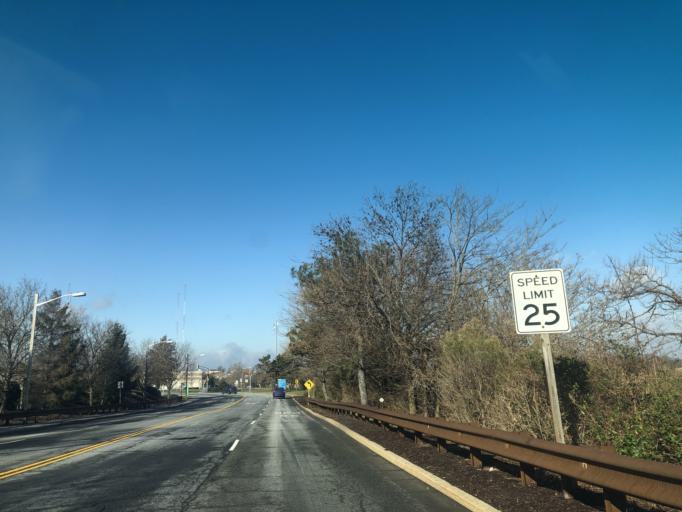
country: US
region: New Jersey
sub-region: Hudson County
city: Secaucus
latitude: 40.7929
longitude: -74.0476
